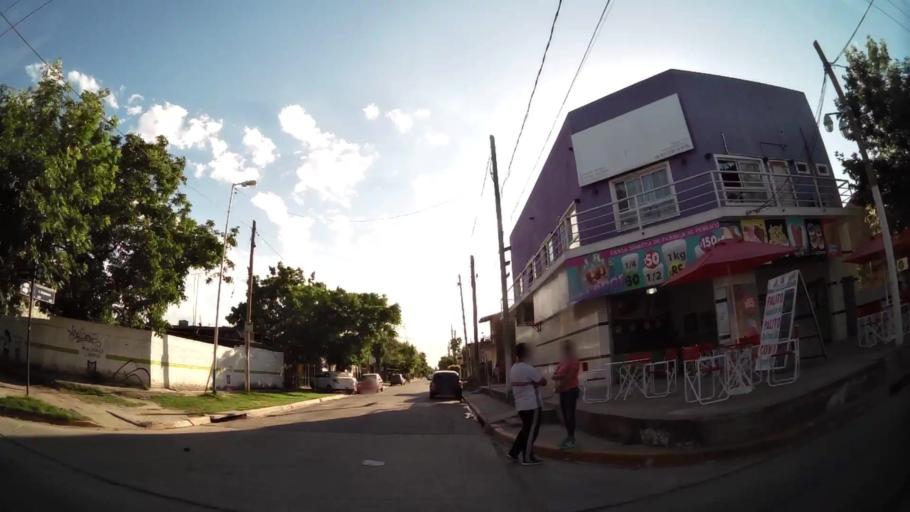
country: AR
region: Buenos Aires
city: Santa Catalina - Dique Lujan
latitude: -34.4970
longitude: -58.7183
